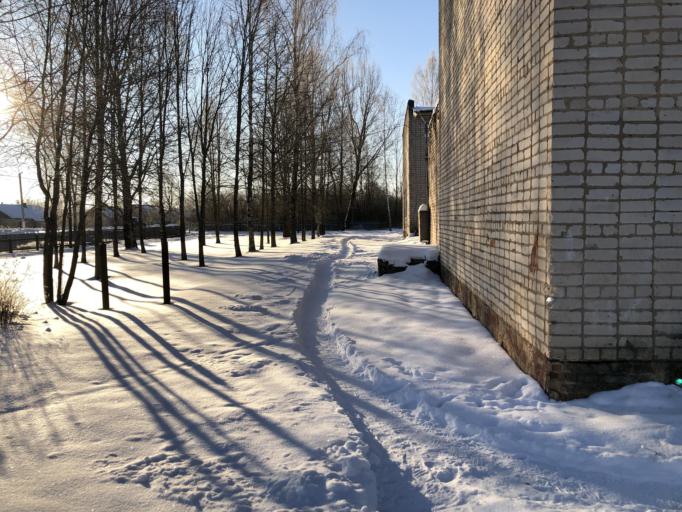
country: RU
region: Smolensk
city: Safonovo
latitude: 55.0866
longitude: 33.0704
